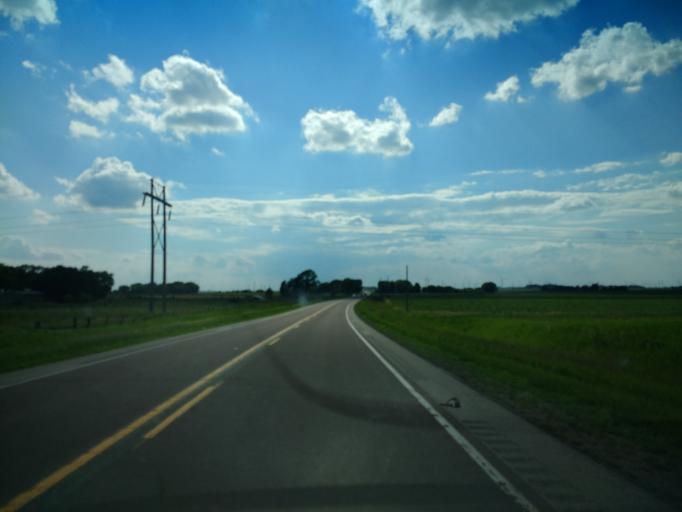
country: US
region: Iowa
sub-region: Clay County
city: Spencer
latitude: 43.1833
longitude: -95.2393
